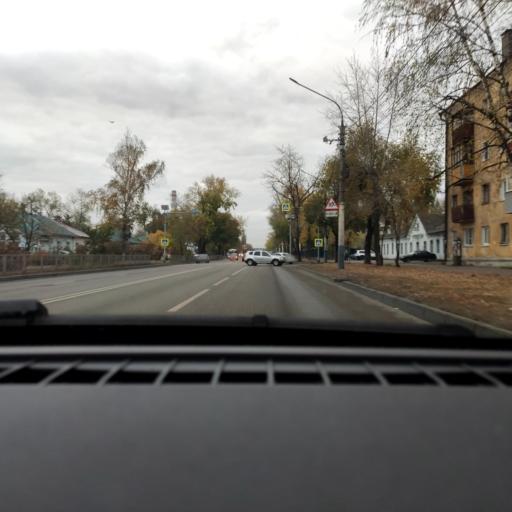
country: RU
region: Voronezj
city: Somovo
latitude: 51.7149
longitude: 39.2748
